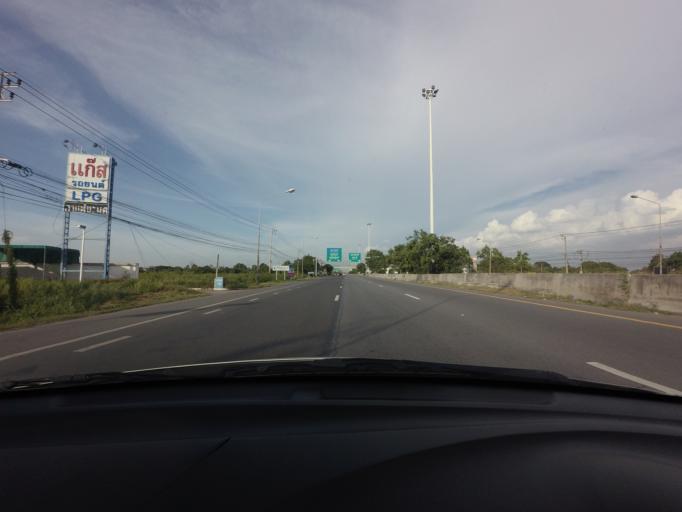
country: TH
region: Nonthaburi
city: Bang Bua Thong
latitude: 13.9494
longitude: 100.4505
